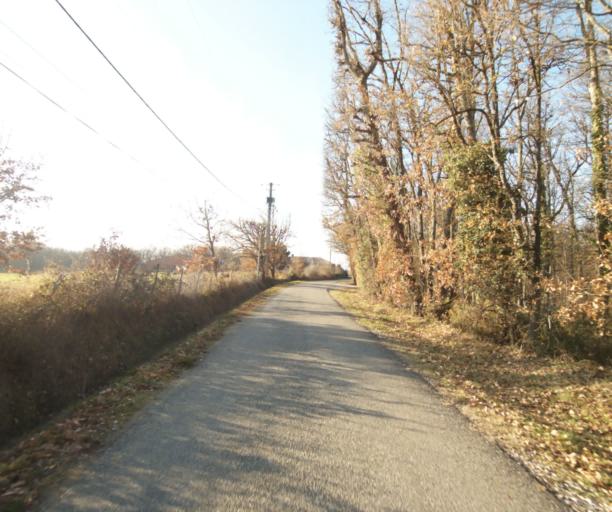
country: FR
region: Midi-Pyrenees
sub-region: Departement du Tarn-et-Garonne
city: Moissac
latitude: 44.1508
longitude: 1.1222
